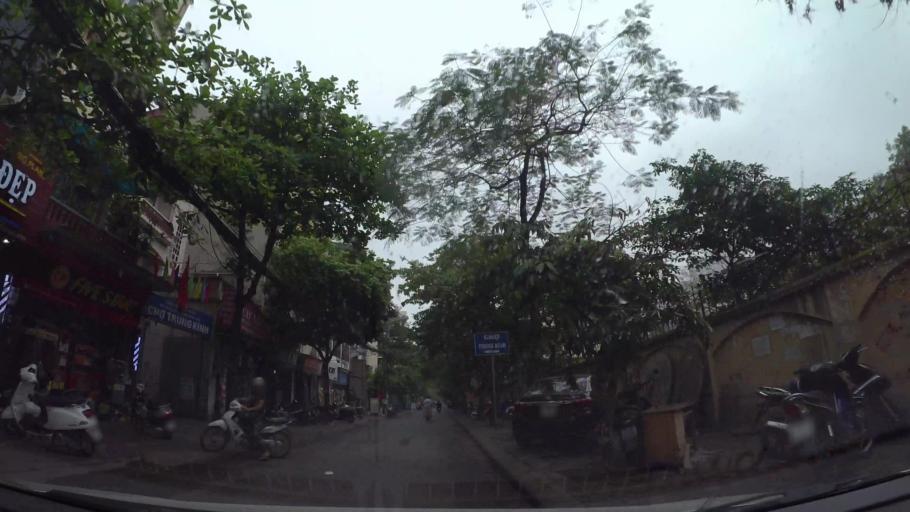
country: VN
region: Ha Noi
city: Cau Giay
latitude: 21.0135
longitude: 105.7996
